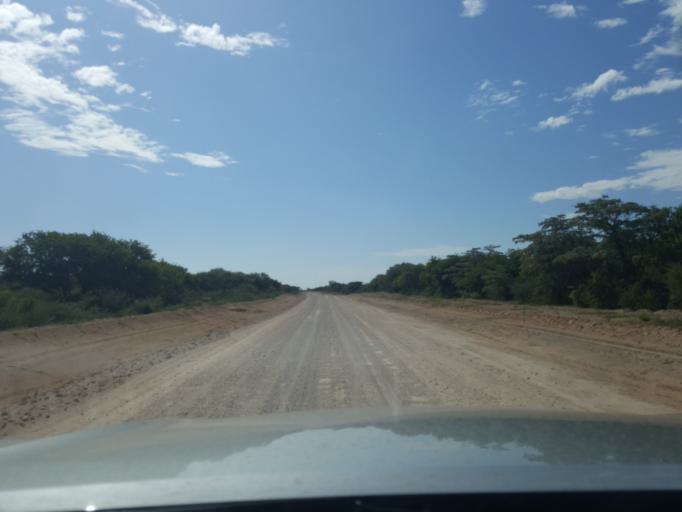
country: BW
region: Kweneng
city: Khudumelapye
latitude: -23.7894
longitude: 24.7861
